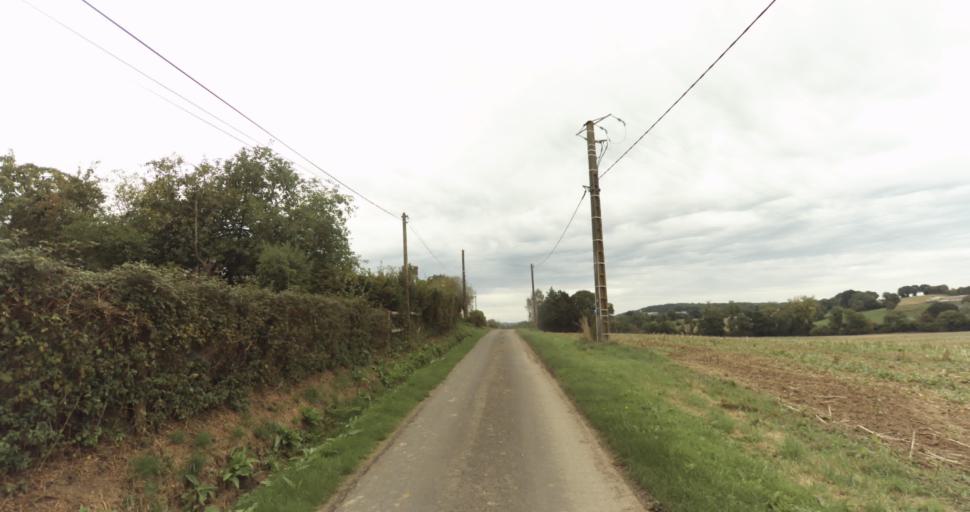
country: FR
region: Lower Normandy
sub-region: Departement de l'Orne
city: Gace
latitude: 48.6855
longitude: 0.2696
